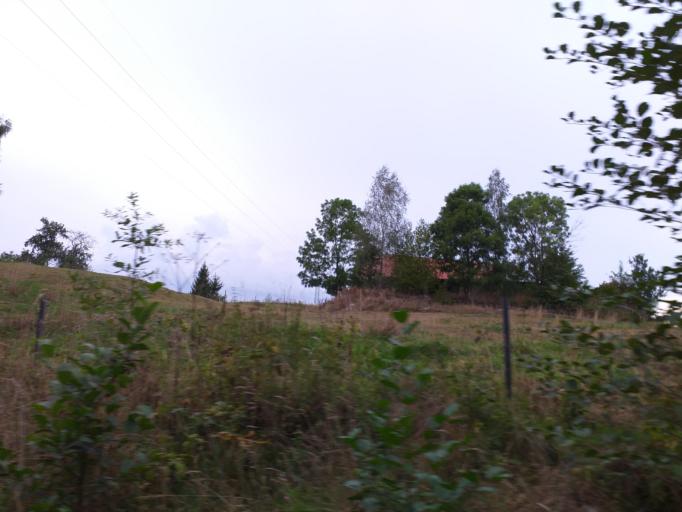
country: PL
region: Lower Silesian Voivodeship
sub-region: Powiat lubanski
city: Lesna
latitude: 51.0172
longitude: 15.3127
